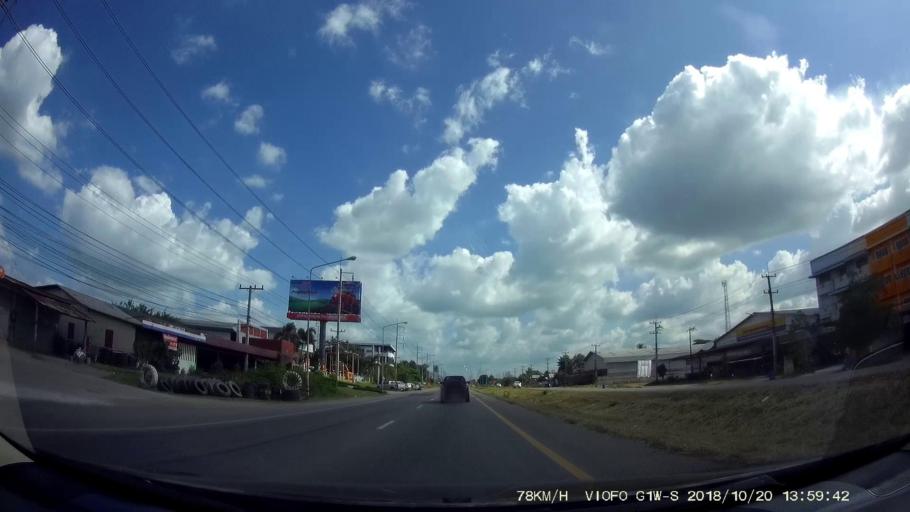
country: TH
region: Khon Kaen
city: Chum Phae
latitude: 16.5221
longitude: 102.1145
